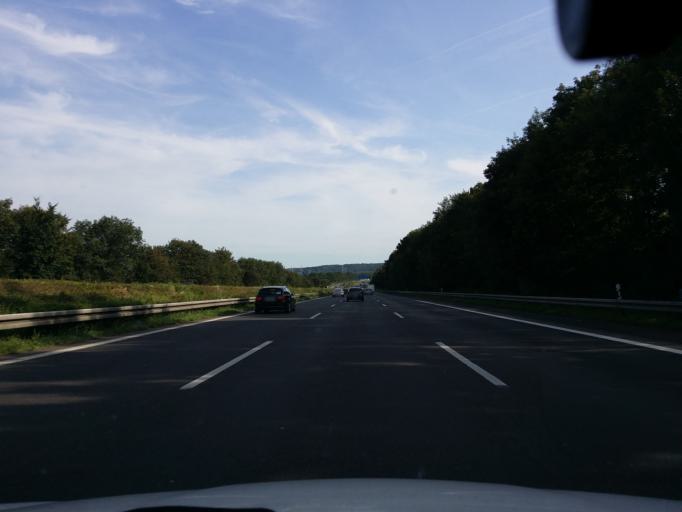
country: DE
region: North Rhine-Westphalia
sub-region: Regierungsbezirk Koln
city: Stossdorf
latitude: 50.7906
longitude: 7.2359
